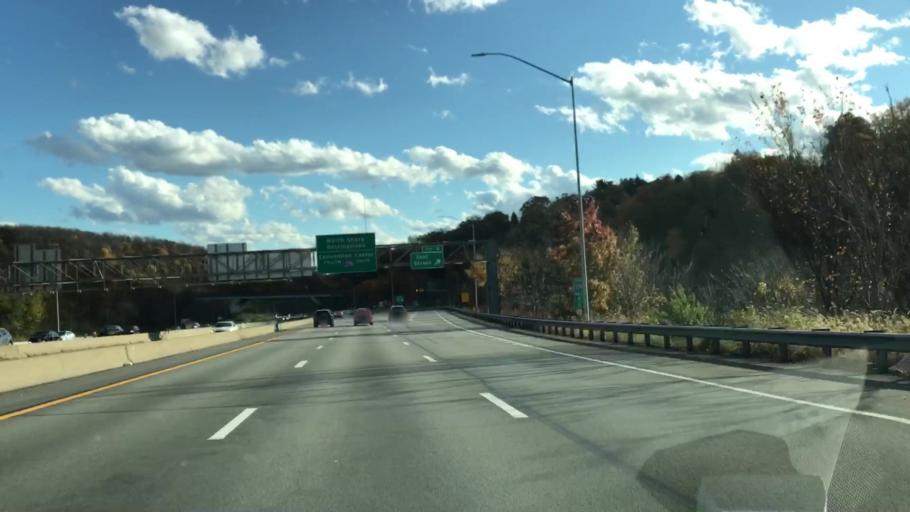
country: US
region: Pennsylvania
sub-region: Allegheny County
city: Millvale
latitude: 40.4884
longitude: -80.0096
